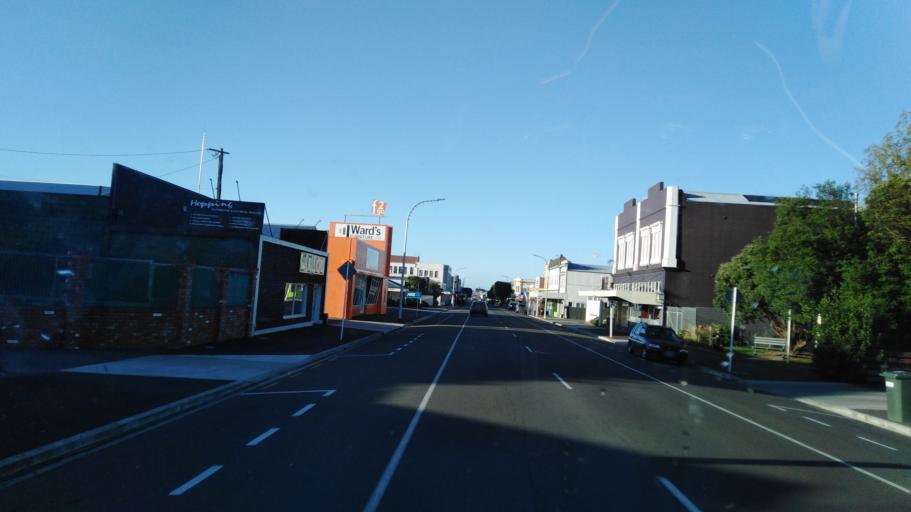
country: NZ
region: Manawatu-Wanganui
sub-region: Rangitikei District
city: Bulls
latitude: -40.0656
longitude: 175.3792
